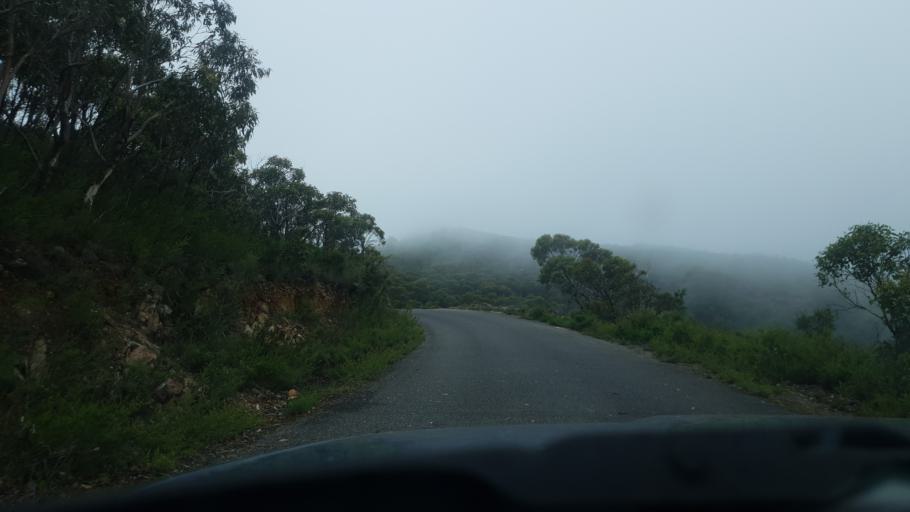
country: AU
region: Victoria
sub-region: Northern Grampians
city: Stawell
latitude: -37.2710
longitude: 142.5807
